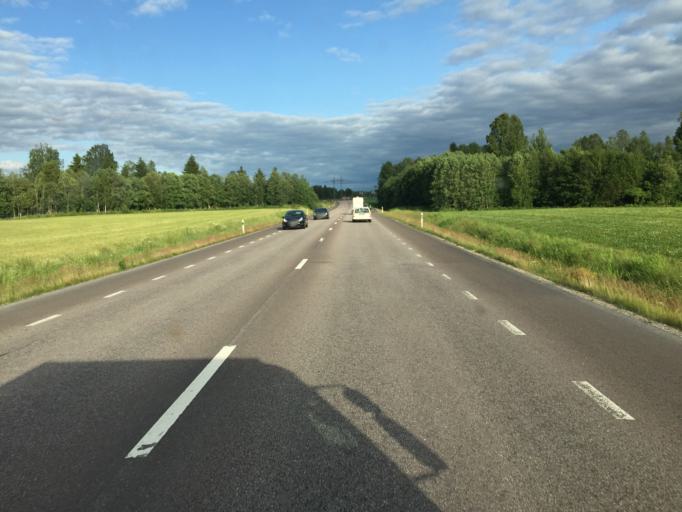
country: SE
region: Dalarna
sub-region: Gagnefs Kommun
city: Djuras
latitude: 60.5534
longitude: 15.1549
